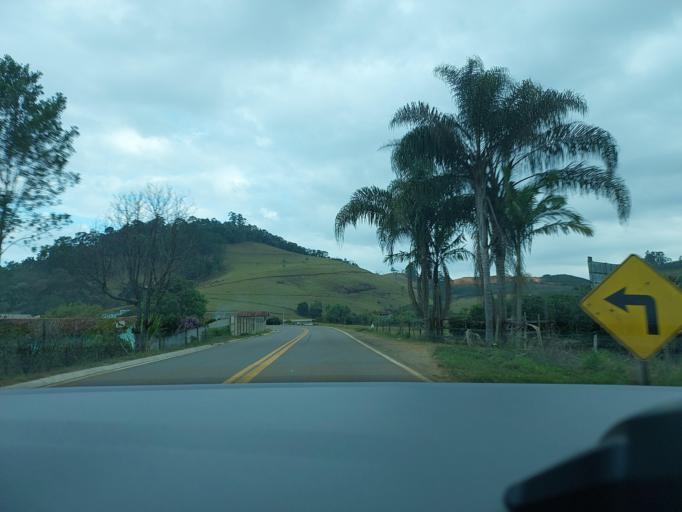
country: BR
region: Minas Gerais
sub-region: Mirai
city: Mirai
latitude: -21.0061
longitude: -42.5533
